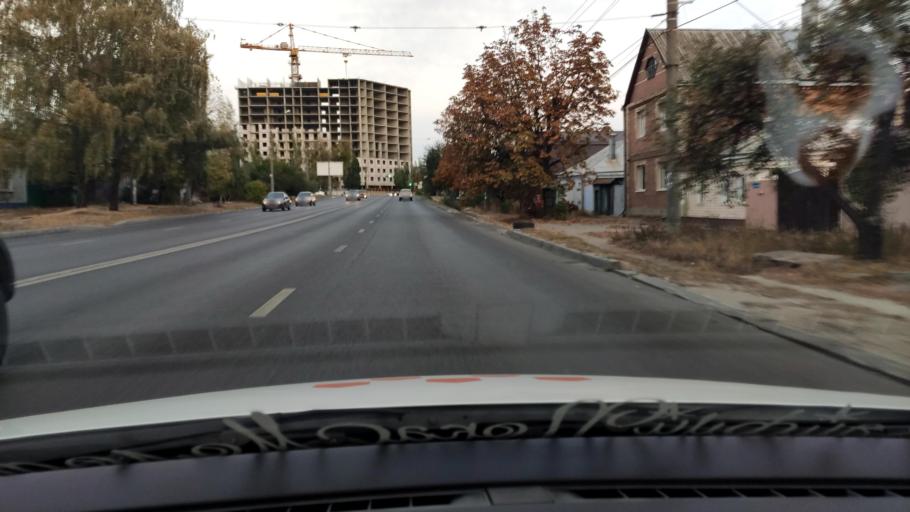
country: RU
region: Voronezj
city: Voronezh
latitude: 51.6957
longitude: 39.1929
